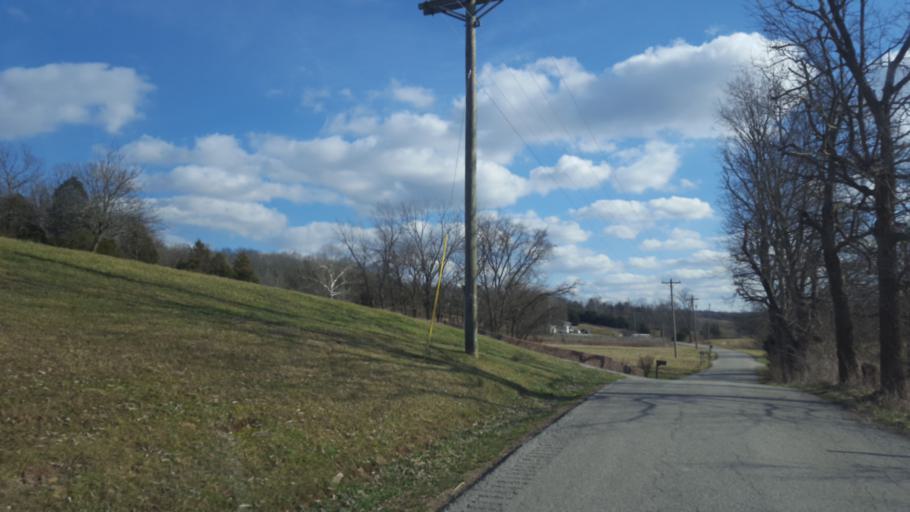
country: US
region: Kentucky
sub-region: Scott County
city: Georgetown
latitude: 38.3153
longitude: -84.5085
